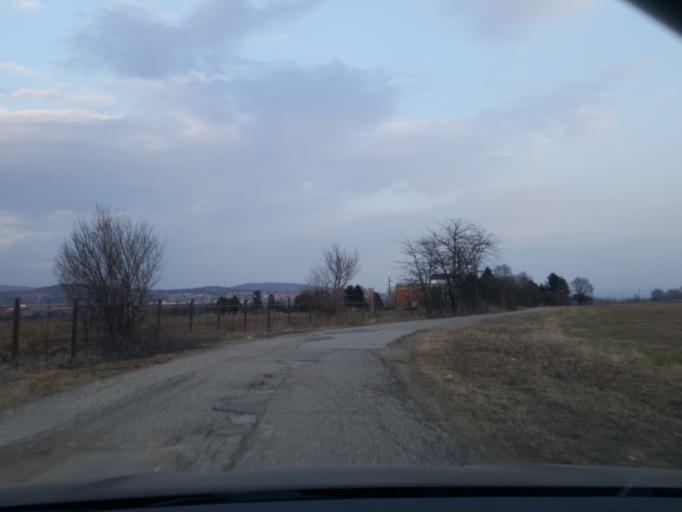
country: RS
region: Central Serbia
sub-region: Nisavski Okrug
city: Aleksinac
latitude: 43.5517
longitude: 21.6676
